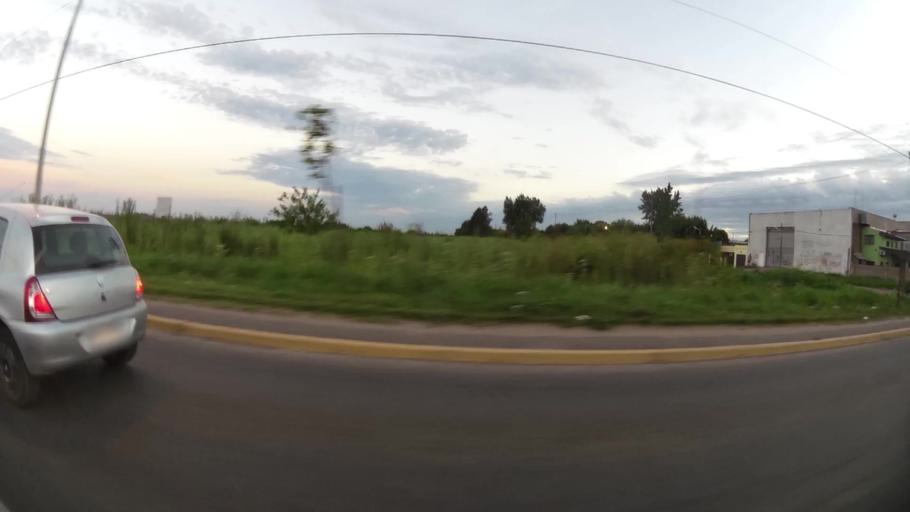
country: AR
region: Buenos Aires
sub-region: Partido de Merlo
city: Merlo
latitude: -34.6749
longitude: -58.7525
